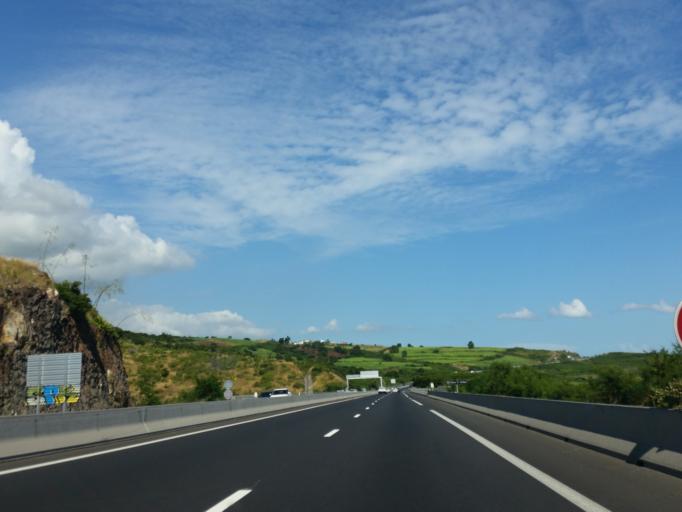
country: RE
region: Reunion
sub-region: Reunion
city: Saint-Paul
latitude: -21.0511
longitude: 55.2483
